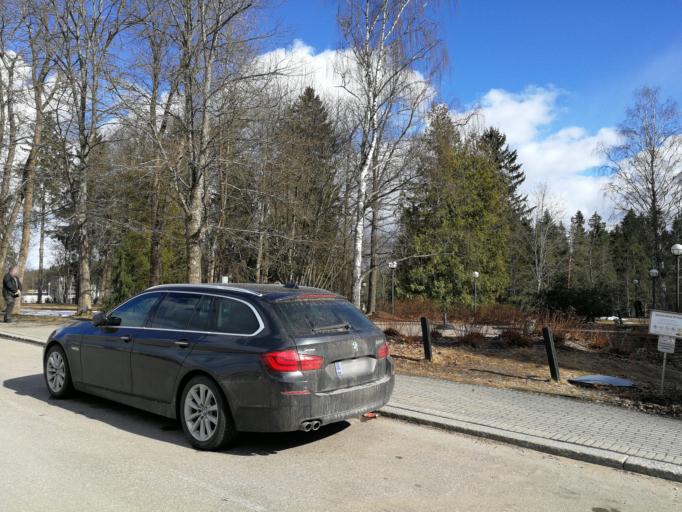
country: FI
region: South Karelia
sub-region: Imatra
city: Imatra
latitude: 61.1694
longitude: 28.7710
